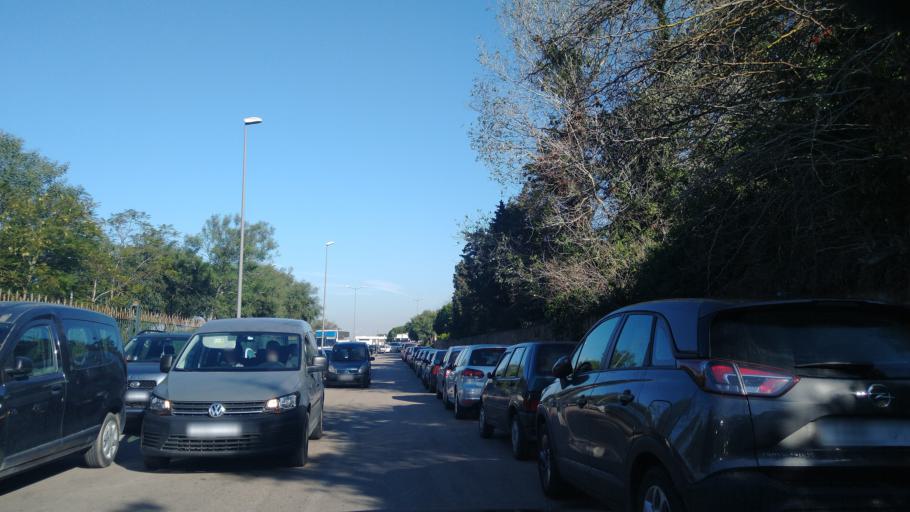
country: MA
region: Rabat-Sale-Zemmour-Zaer
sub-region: Rabat
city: Rabat
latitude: 33.9826
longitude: -6.8536
